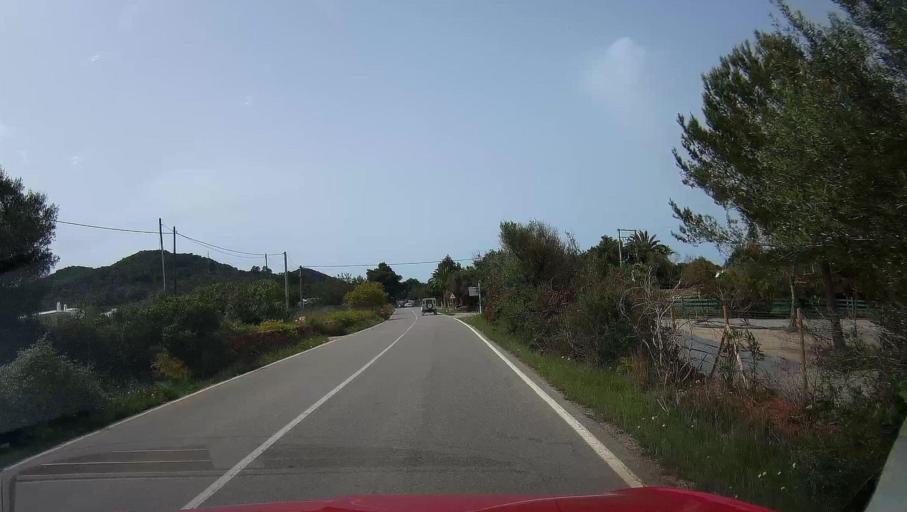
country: ES
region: Balearic Islands
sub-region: Illes Balears
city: Santa Eularia des Riu
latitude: 38.9886
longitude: 1.4886
